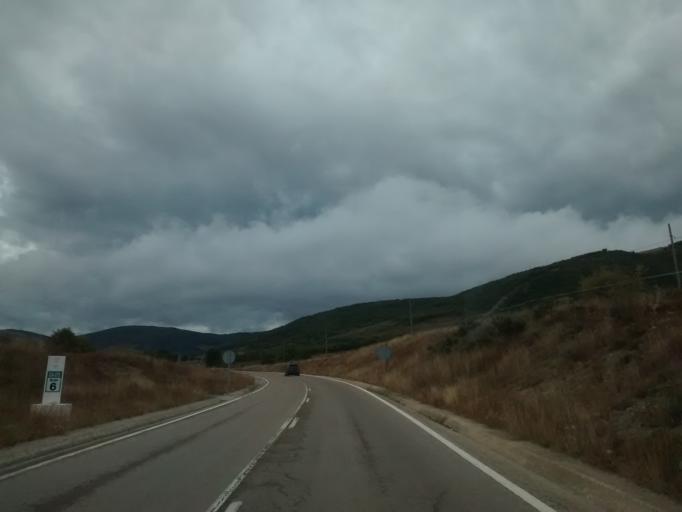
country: ES
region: Cantabria
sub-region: Provincia de Cantabria
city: Mataporquera
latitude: 42.8807
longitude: -4.0711
